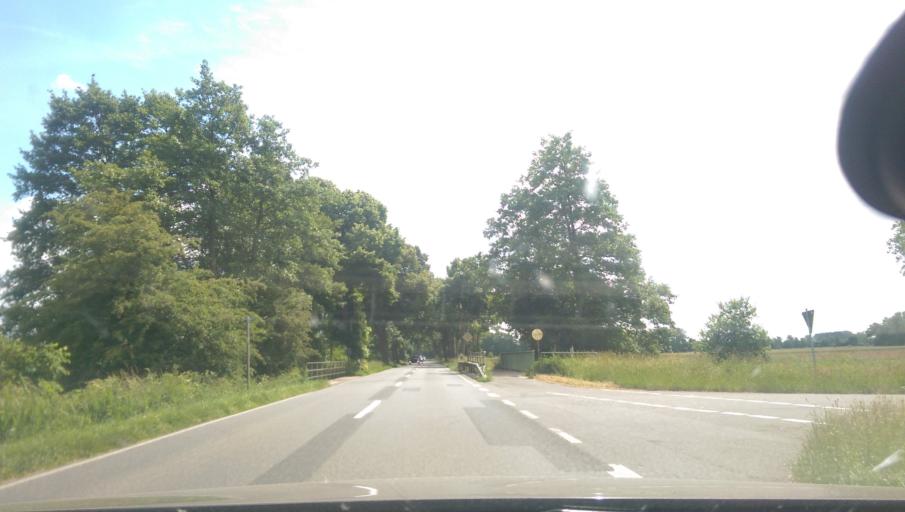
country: DE
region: Lower Saxony
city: Oyten
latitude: 53.1041
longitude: 9.0556
